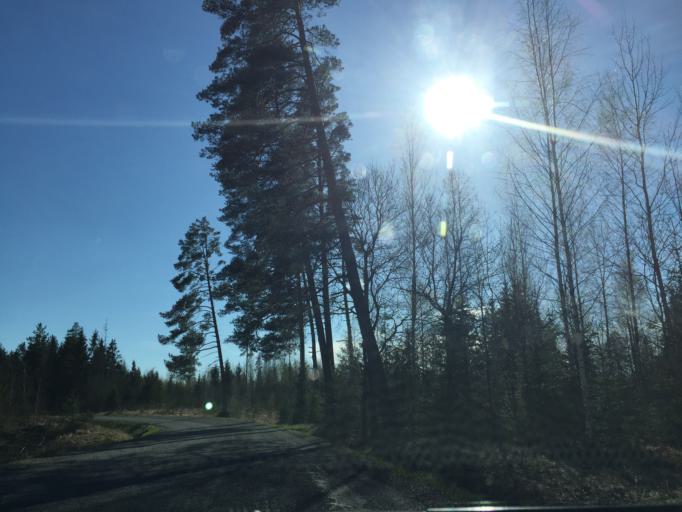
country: EE
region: Valgamaa
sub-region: Valga linn
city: Valga
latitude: 57.8484
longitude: 26.2494
